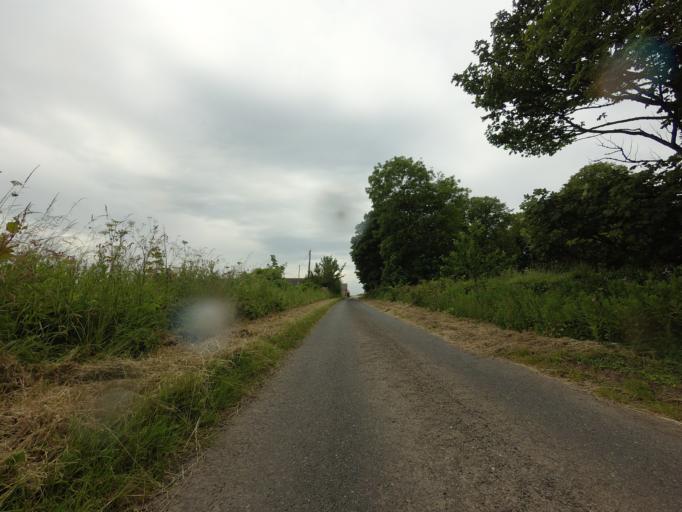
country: GB
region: Scotland
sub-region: Aberdeenshire
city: Portsoy
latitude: 57.6766
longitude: -2.6625
